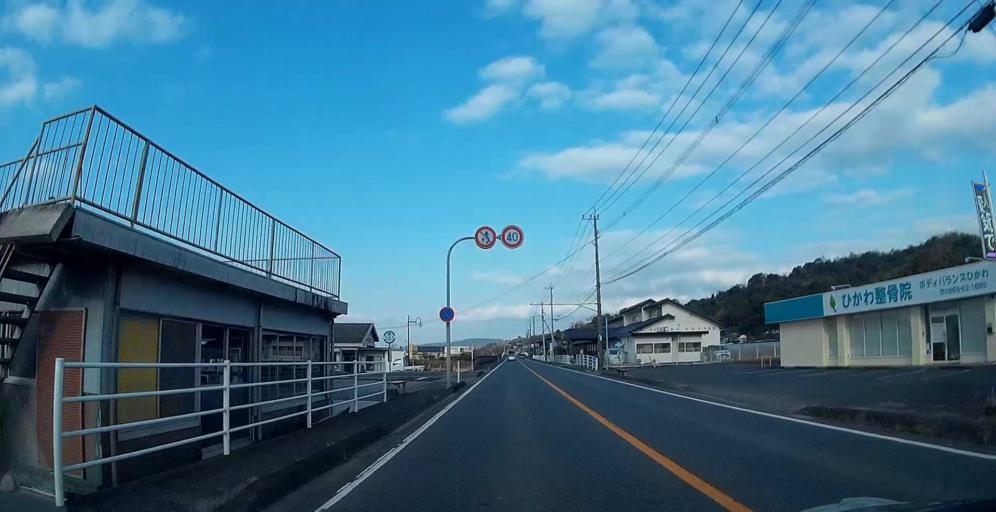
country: JP
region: Kumamoto
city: Matsubase
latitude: 32.5613
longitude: 130.6847
